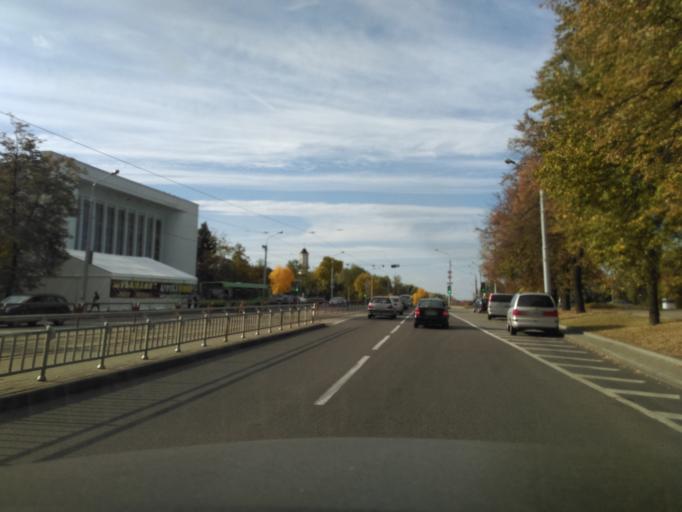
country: BY
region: Minsk
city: Minsk
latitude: 53.8899
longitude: 27.6149
